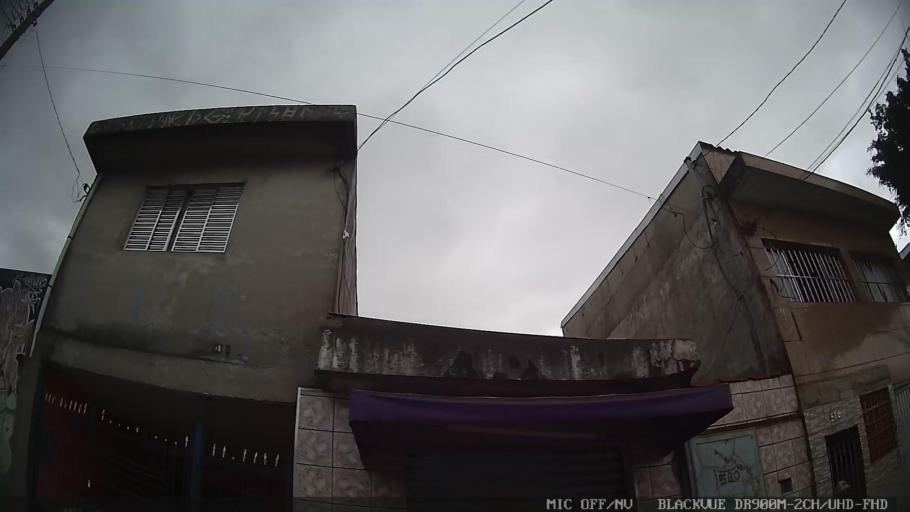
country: BR
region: Sao Paulo
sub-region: Osasco
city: Osasco
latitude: -23.4704
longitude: -46.7138
